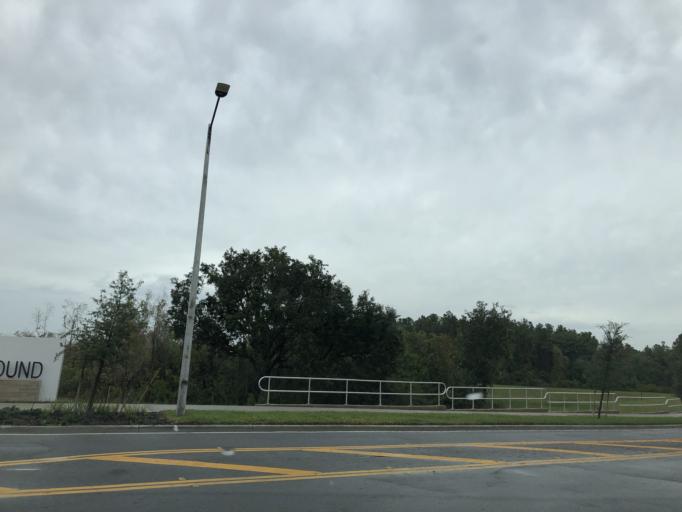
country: US
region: Florida
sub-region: Orange County
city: Doctor Phillips
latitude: 28.4450
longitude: -81.4796
